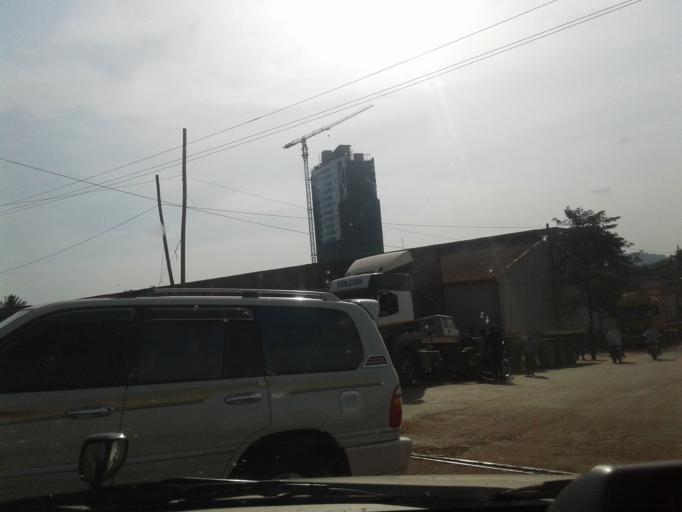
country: UG
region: Central Region
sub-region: Wakiso District
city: Kireka
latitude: 0.3310
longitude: 32.6224
